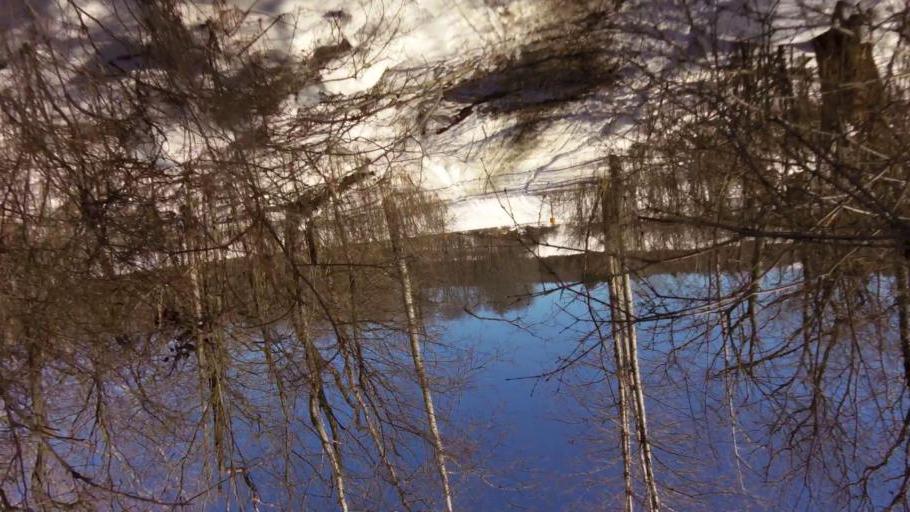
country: US
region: New York
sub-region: Allegany County
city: Houghton
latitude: 42.3621
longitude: -78.1540
